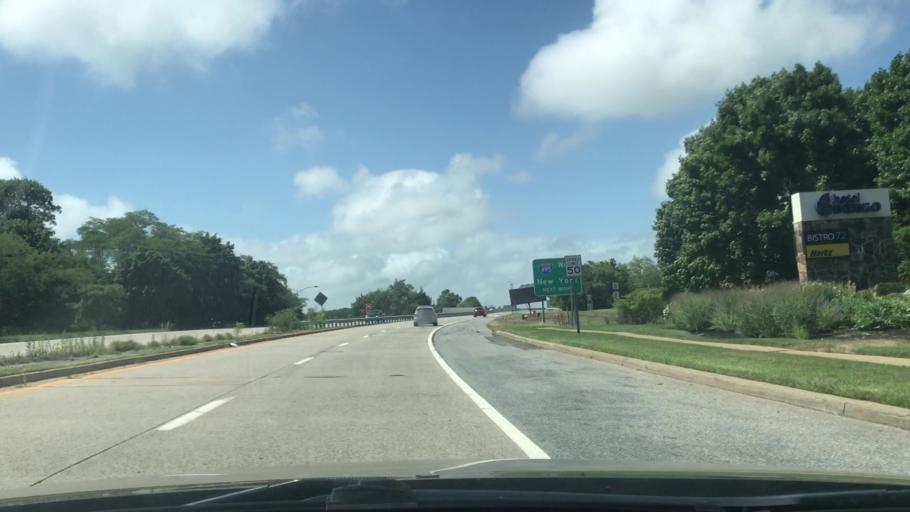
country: US
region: New York
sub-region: Suffolk County
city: Calverton
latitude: 40.9187
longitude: -72.7213
